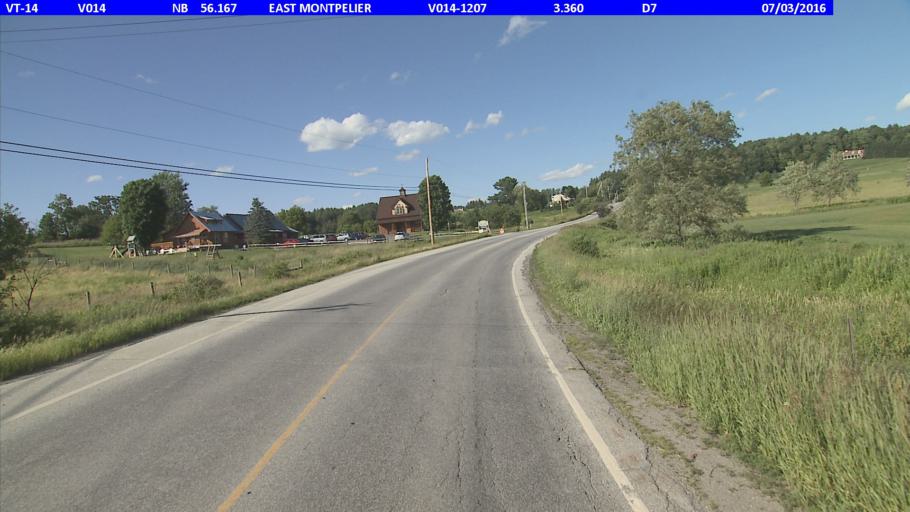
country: US
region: Vermont
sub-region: Washington County
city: Barre
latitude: 44.2802
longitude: -72.4739
